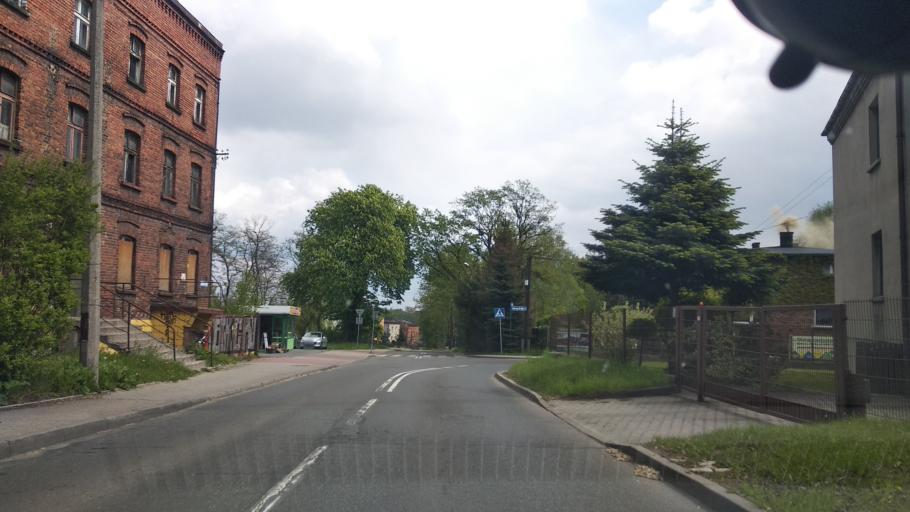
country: PL
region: Silesian Voivodeship
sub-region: Katowice
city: Katowice
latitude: 50.2503
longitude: 18.9835
